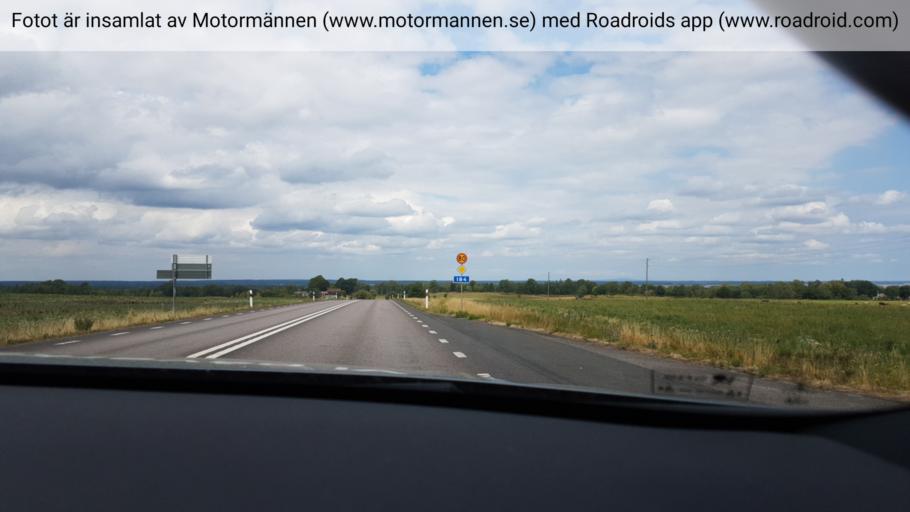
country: SE
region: Vaestra Goetaland
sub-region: Falkopings Kommun
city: Falkoeping
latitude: 58.2354
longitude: 13.5480
